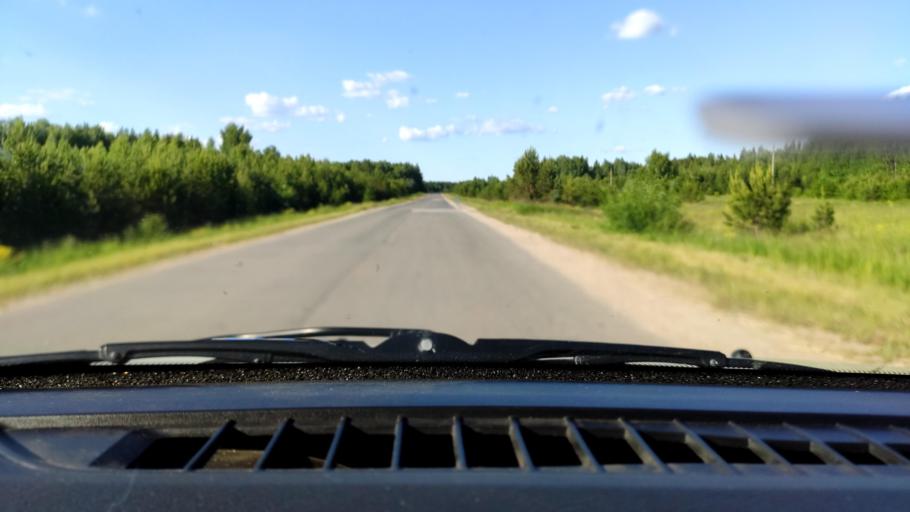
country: RU
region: Perm
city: Uinskoye
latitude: 57.1151
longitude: 56.6689
